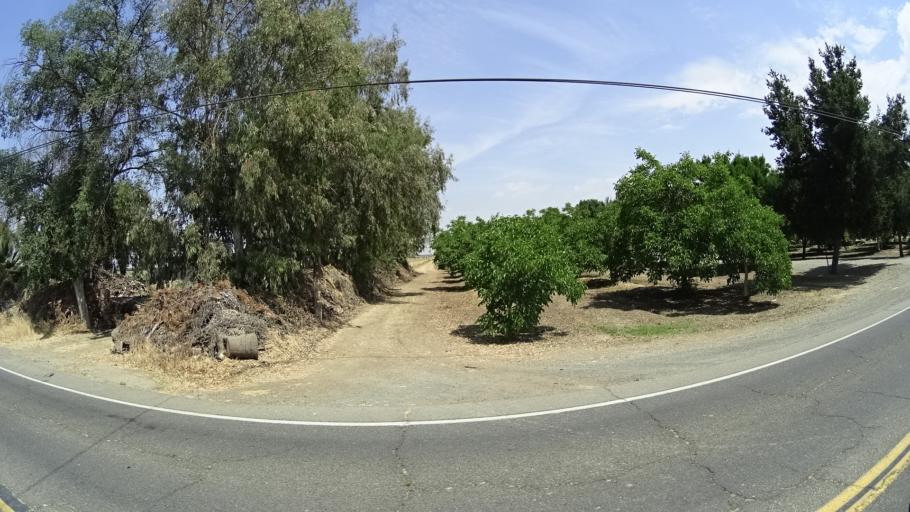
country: US
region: California
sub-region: Kings County
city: Armona
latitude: 36.3280
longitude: -119.7385
